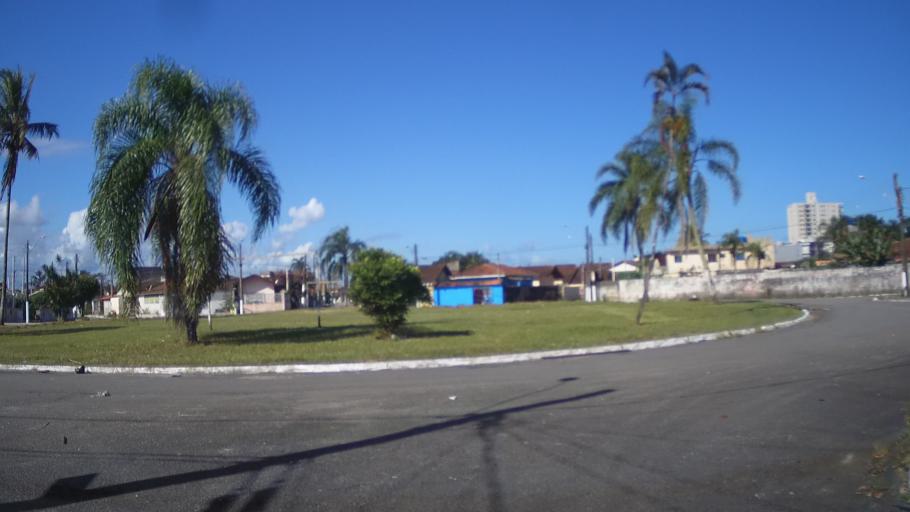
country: BR
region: Sao Paulo
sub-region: Mongagua
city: Mongagua
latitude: -24.0607
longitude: -46.5539
